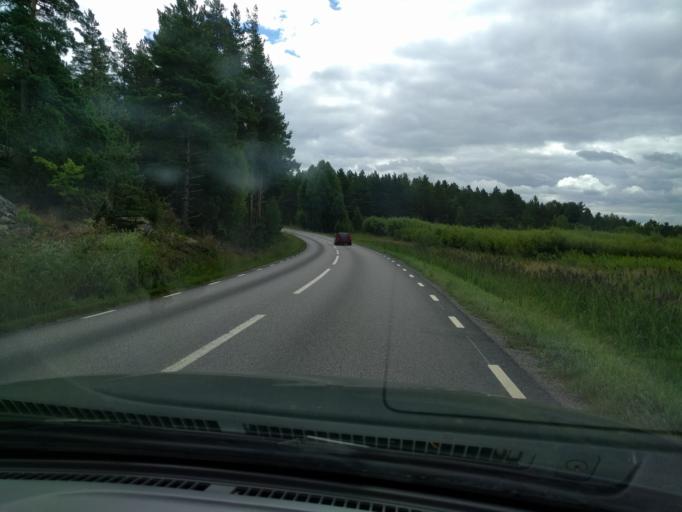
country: SE
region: Soedermanland
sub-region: Nykopings Kommun
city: Svalsta
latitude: 58.5307
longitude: 16.7486
